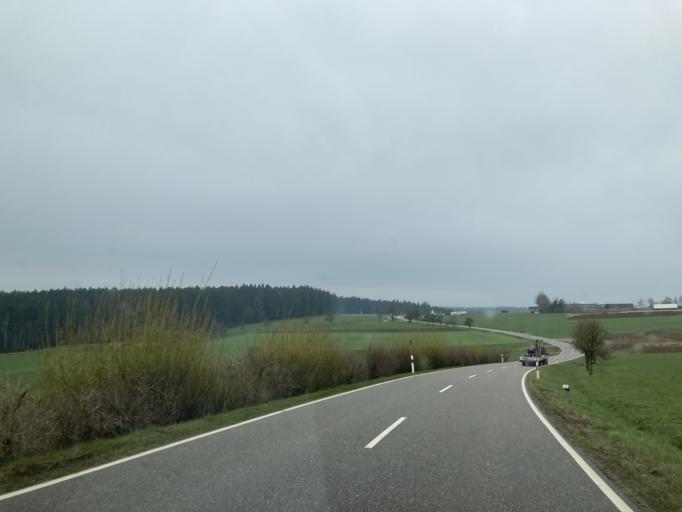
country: DE
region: Baden-Wuerttemberg
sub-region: Freiburg Region
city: Dornhan
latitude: 48.3509
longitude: 8.4703
